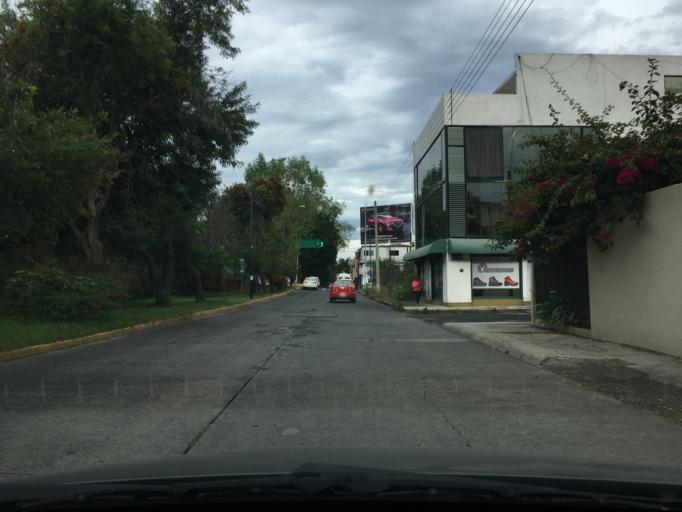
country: MX
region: Michoacan
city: Morelia
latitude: 19.6861
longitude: -101.1722
